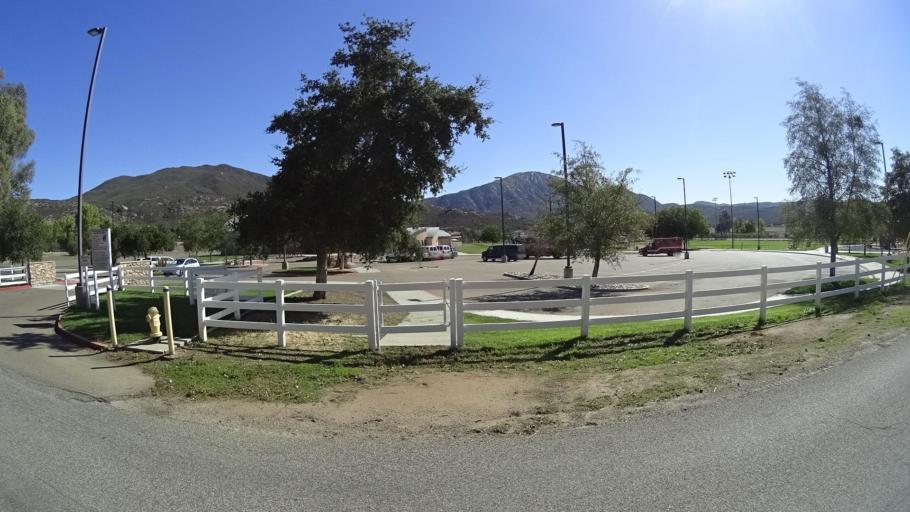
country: US
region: California
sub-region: San Diego County
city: Alpine
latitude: 32.8570
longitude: -116.6981
